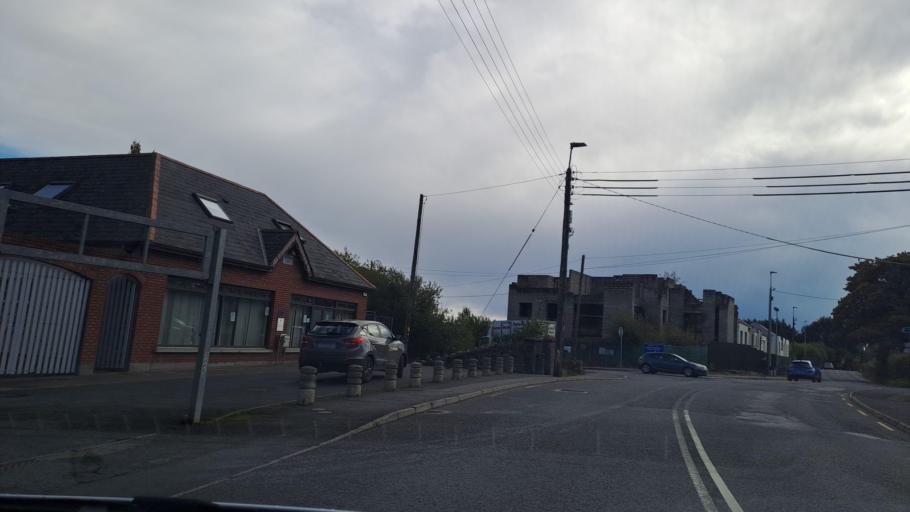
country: IE
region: Ulster
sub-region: County Monaghan
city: Carrickmacross
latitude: 53.9722
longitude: -6.7180
